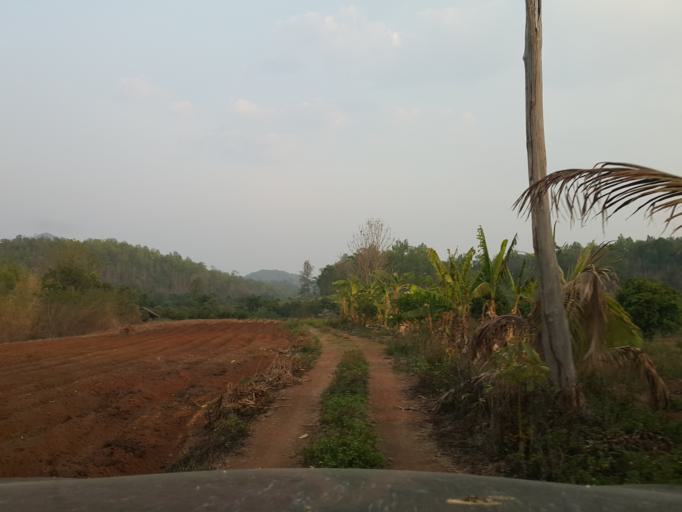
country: TH
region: Lamphun
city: Thung Hua Chang
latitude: 17.9111
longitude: 99.0748
